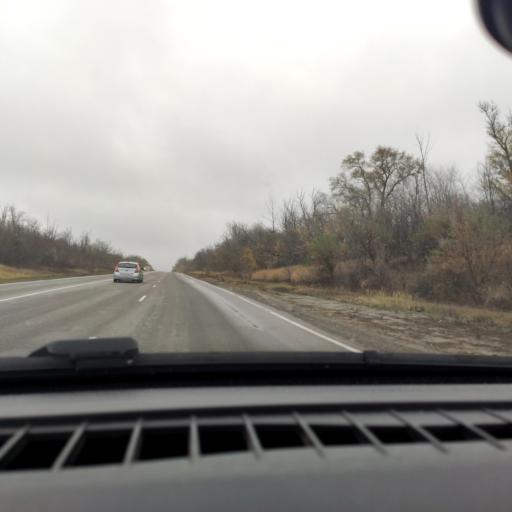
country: RU
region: Voronezj
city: Uryv-Pokrovka
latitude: 51.1390
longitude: 39.0539
